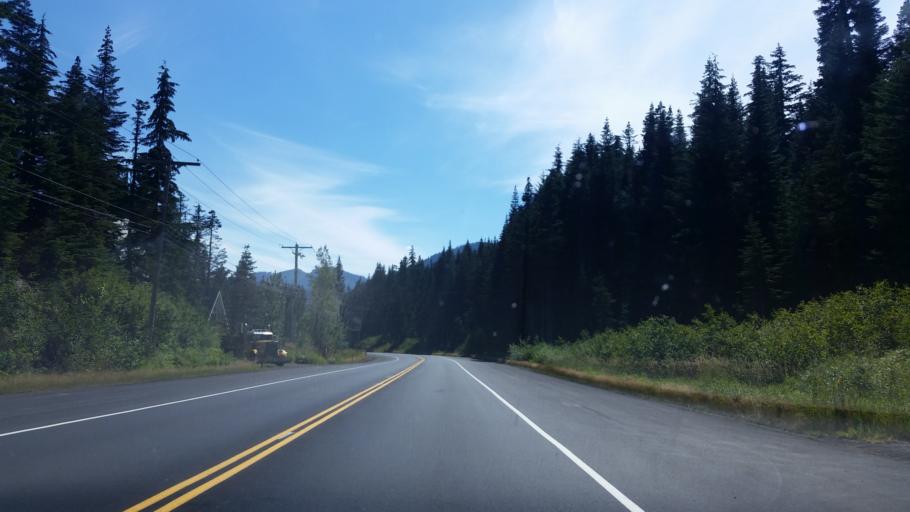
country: US
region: Washington
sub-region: King County
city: Tanner
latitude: 47.4157
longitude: -121.4134
